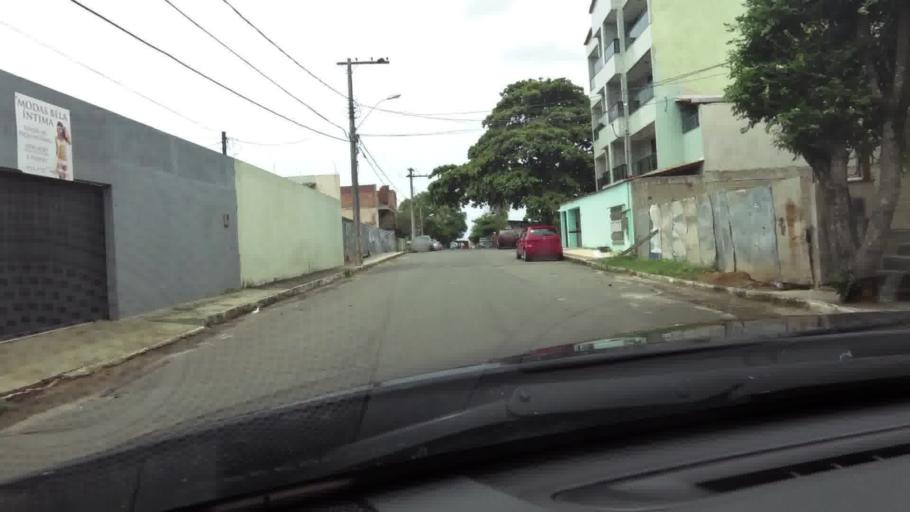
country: BR
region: Espirito Santo
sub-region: Guarapari
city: Guarapari
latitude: -20.6568
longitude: -40.4986
